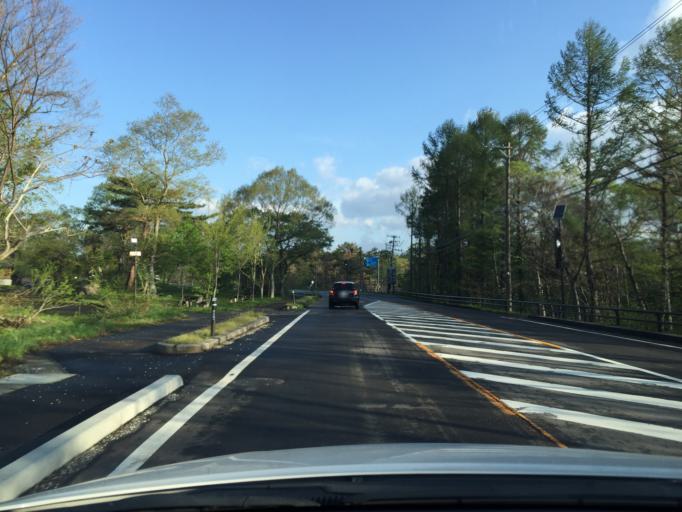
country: JP
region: Fukushima
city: Inawashiro
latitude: 37.6553
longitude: 140.0930
